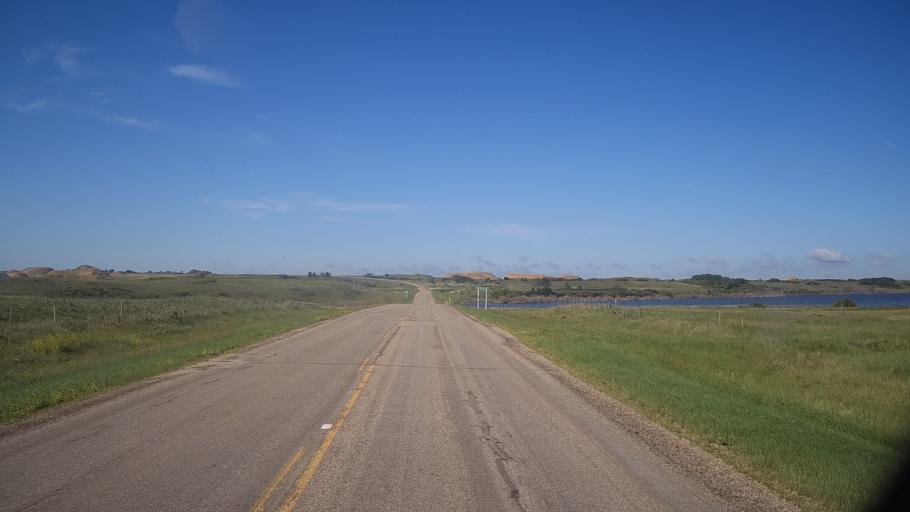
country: CA
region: Saskatchewan
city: Watrous
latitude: 51.7129
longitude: -105.3704
